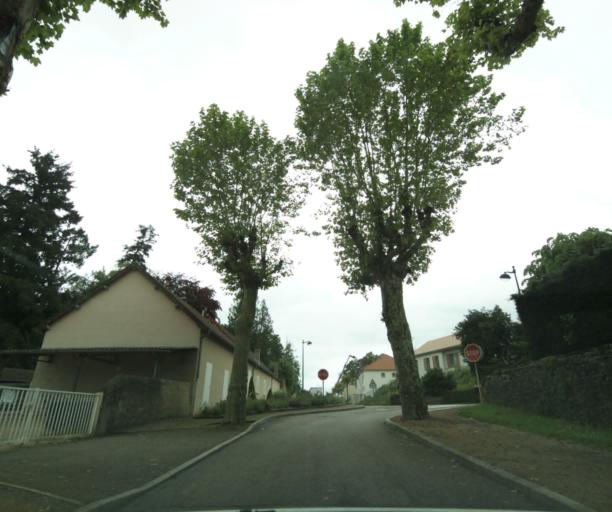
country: FR
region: Bourgogne
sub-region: Departement de Saone-et-Loire
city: Charolles
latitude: 46.4383
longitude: 4.2719
